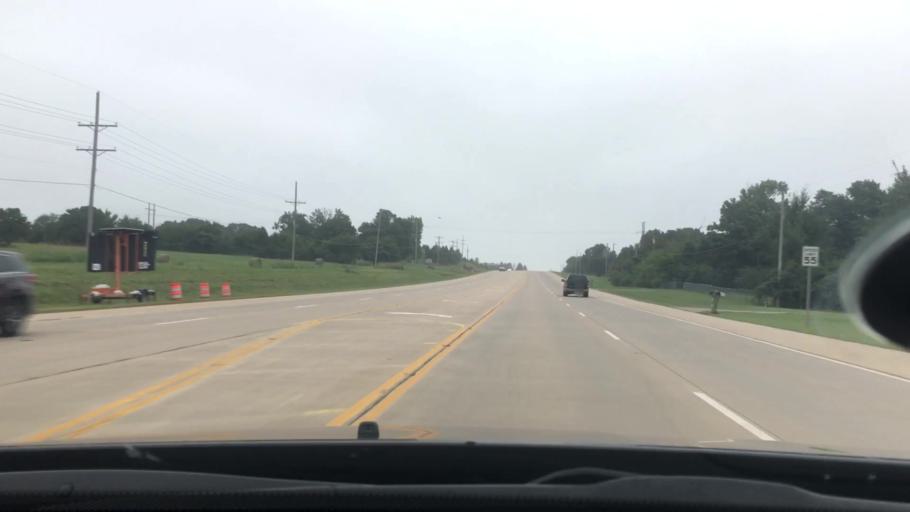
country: US
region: Oklahoma
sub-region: Seminole County
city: Seminole
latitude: 35.2615
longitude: -96.6710
